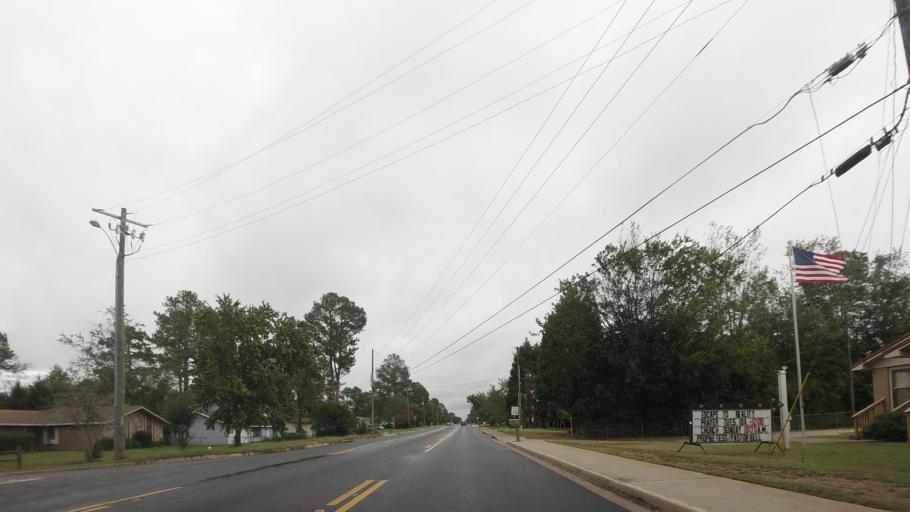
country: US
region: Georgia
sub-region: Houston County
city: Warner Robins
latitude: 32.5746
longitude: -83.6463
